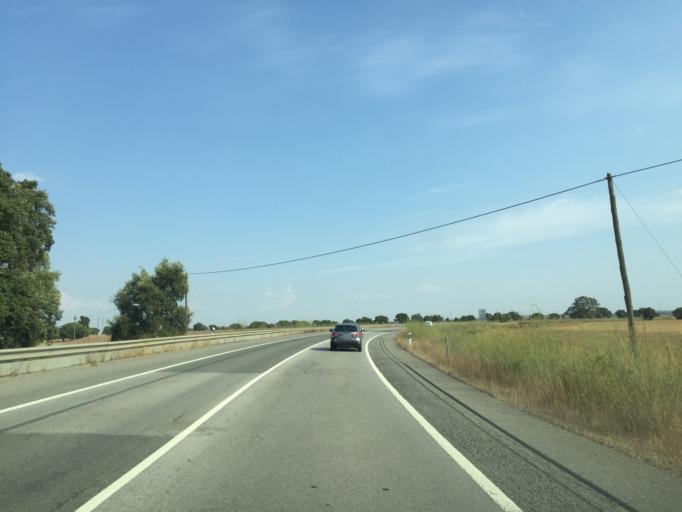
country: PT
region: Beja
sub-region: Aljustrel
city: Aljustrel
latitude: 37.9367
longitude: -8.3620
